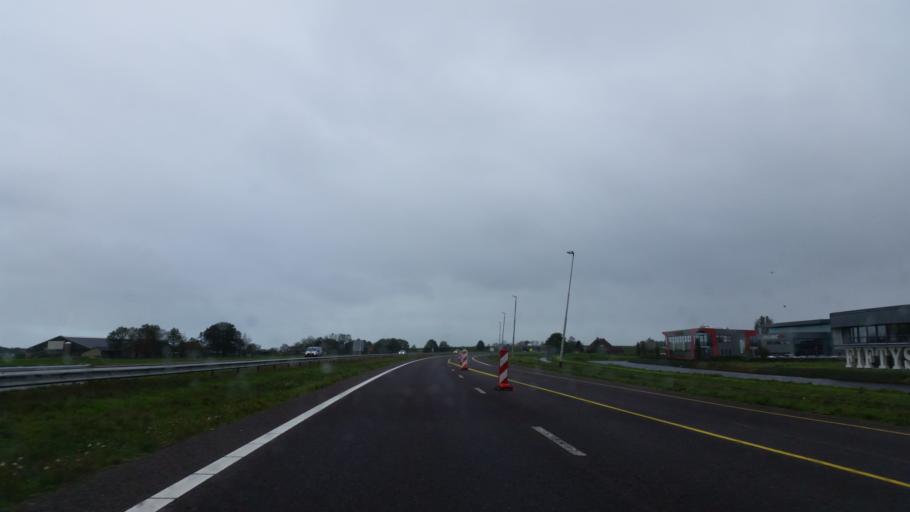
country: NL
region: Friesland
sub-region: Gemeente Skarsterlan
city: Joure
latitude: 52.9575
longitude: 5.7770
